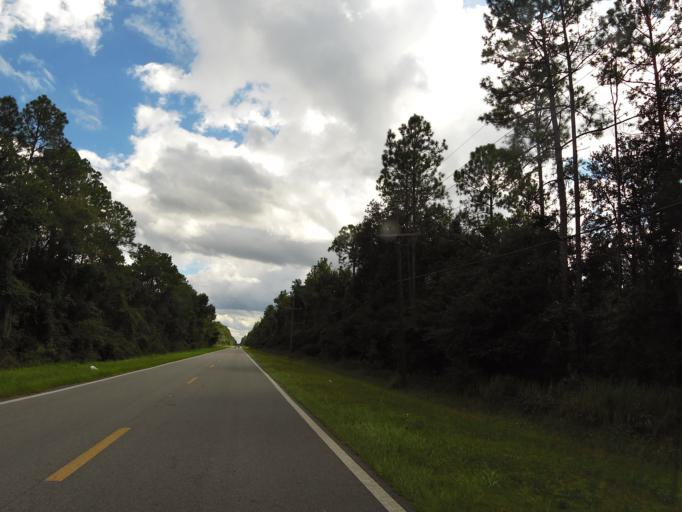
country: US
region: Florida
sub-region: Saint Johns County
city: Saint Augustine
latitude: 29.8895
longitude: -81.4947
